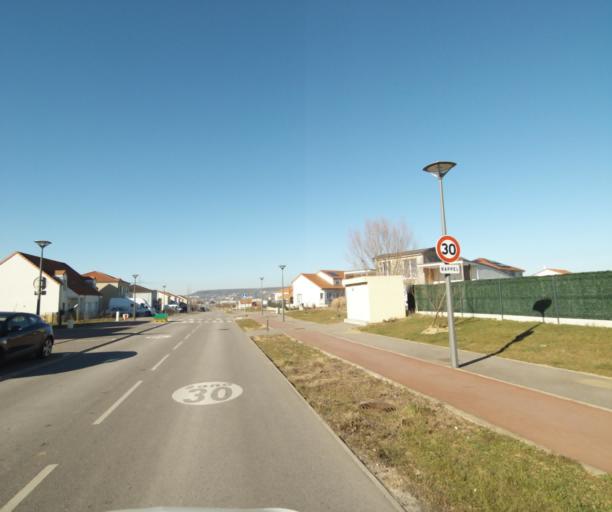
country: FR
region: Lorraine
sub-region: Departement de Meurthe-et-Moselle
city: Tomblaine
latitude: 48.6769
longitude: 6.2287
